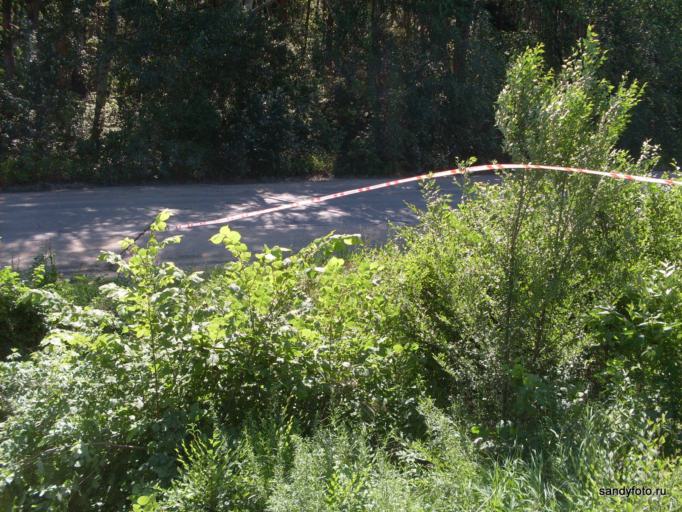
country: RU
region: Chelyabinsk
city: Troitsk
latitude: 54.0509
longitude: 61.6177
